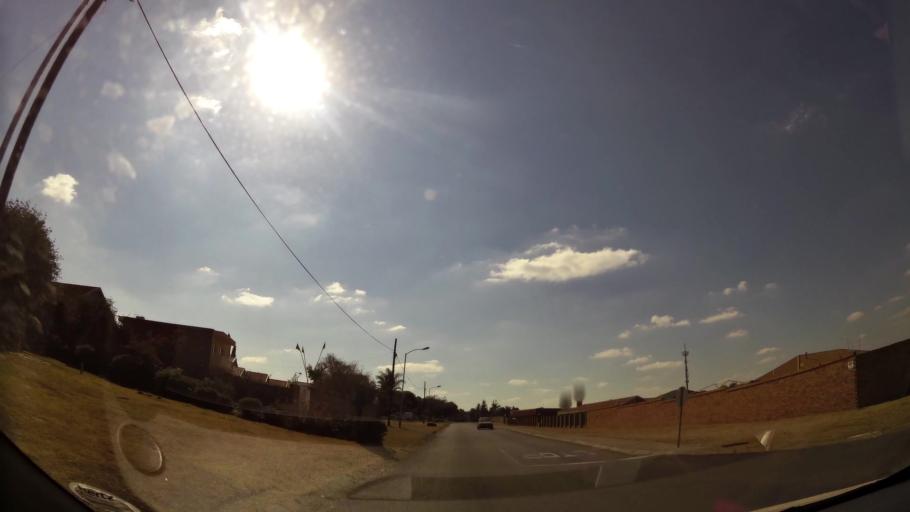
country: ZA
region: Gauteng
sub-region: West Rand District Municipality
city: Randfontein
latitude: -26.1711
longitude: 27.7474
